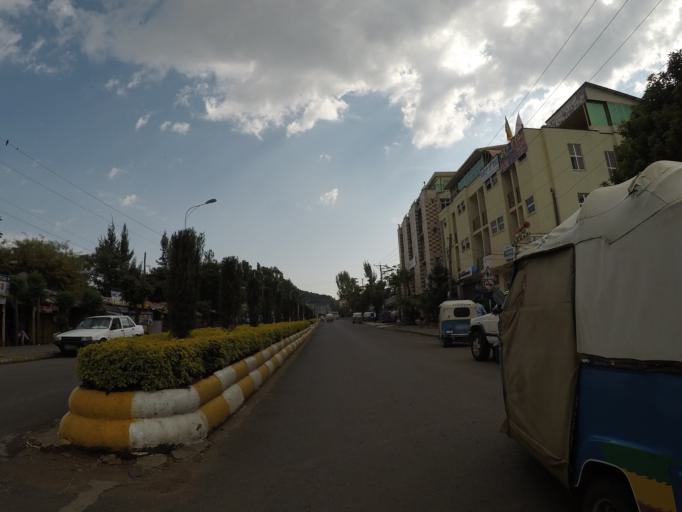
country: ET
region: Amhara
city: Gondar
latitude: 12.5974
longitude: 37.4499
